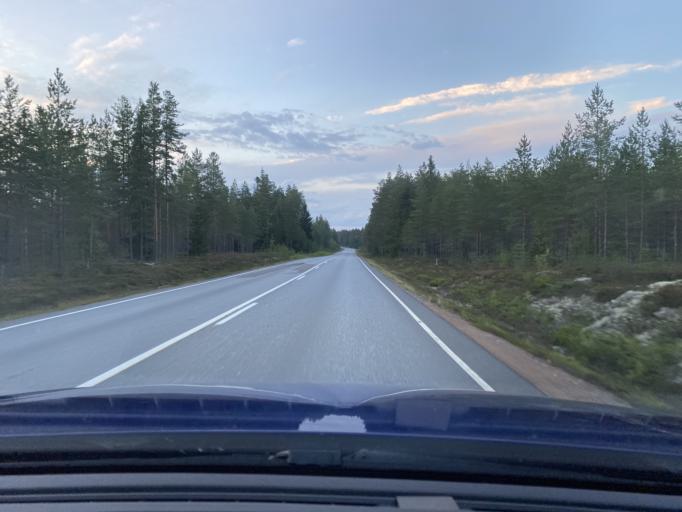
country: FI
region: Satakunta
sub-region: Pohjois-Satakunta
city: Honkajoki
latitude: 62.0328
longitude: 22.2371
